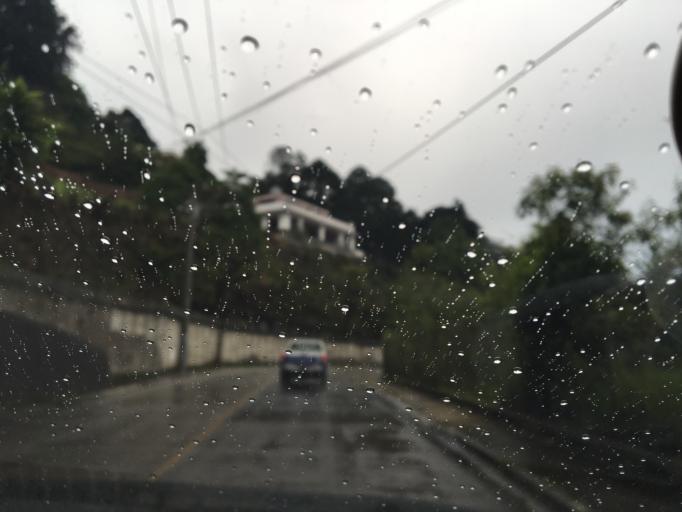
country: GT
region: Guatemala
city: Santa Catarina Pinula
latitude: 14.5560
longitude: -90.4914
